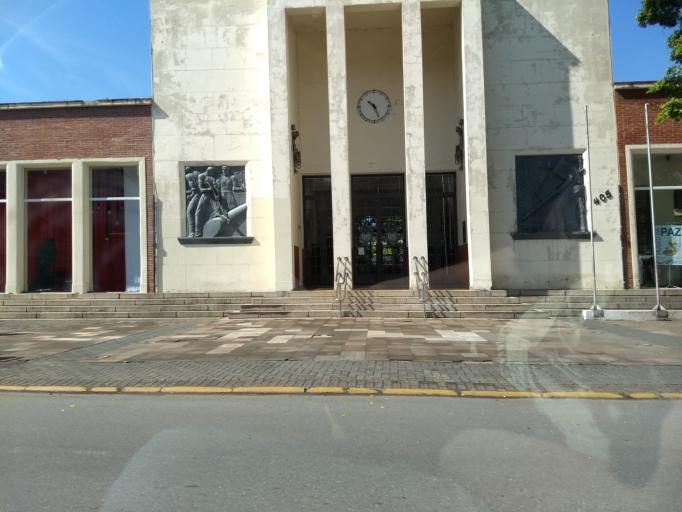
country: BR
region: Santa Catarina
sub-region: Jaragua Do Sul
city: Jaragua do Sul
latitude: -26.4797
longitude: -49.0860
